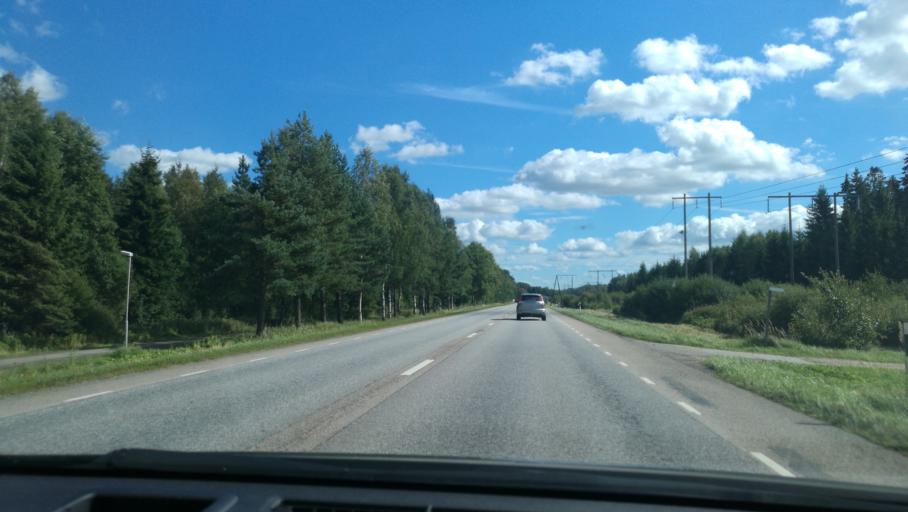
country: SE
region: Vaestra Goetaland
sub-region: Lidkopings Kommun
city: Vinninga
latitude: 58.4928
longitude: 13.2236
